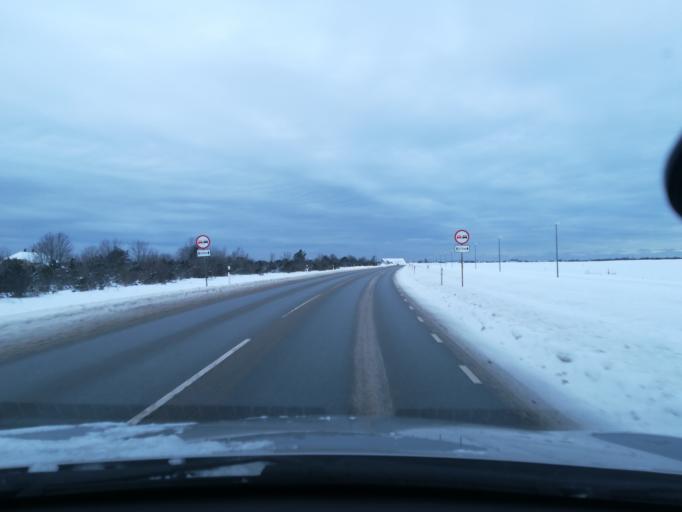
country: EE
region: Harju
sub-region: Harku vald
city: Tabasalu
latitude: 59.4435
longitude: 24.4852
